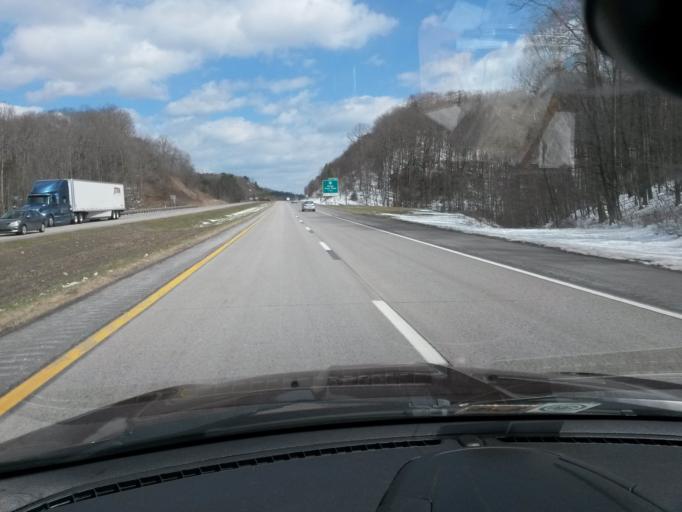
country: US
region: West Virginia
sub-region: Raleigh County
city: Shady Spring
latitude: 37.7669
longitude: -81.0104
